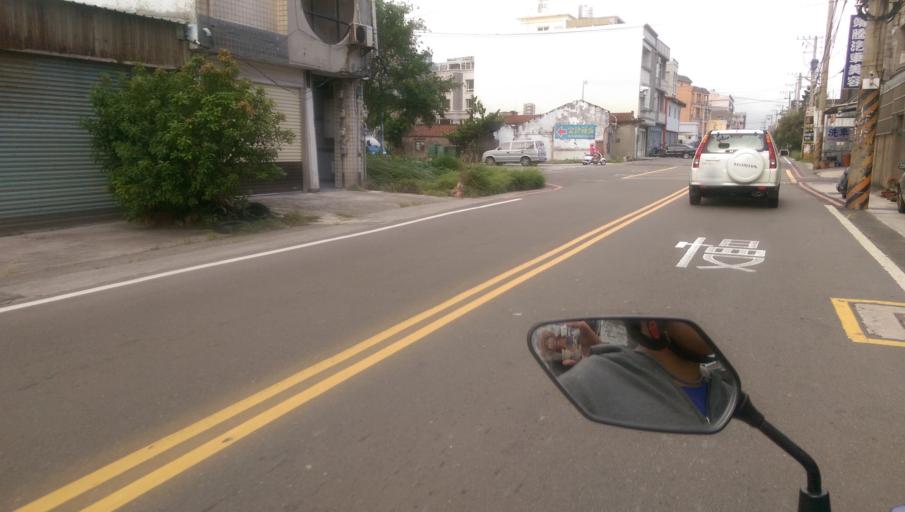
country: TW
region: Taiwan
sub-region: Hsinchu
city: Hsinchu
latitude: 24.8318
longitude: 120.9291
